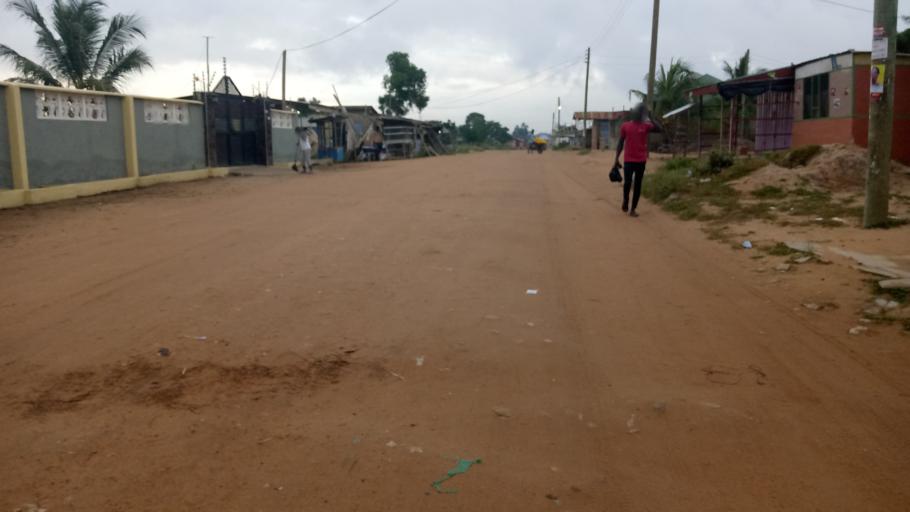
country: GH
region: Central
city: Kasoa
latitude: 5.5000
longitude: -0.4103
